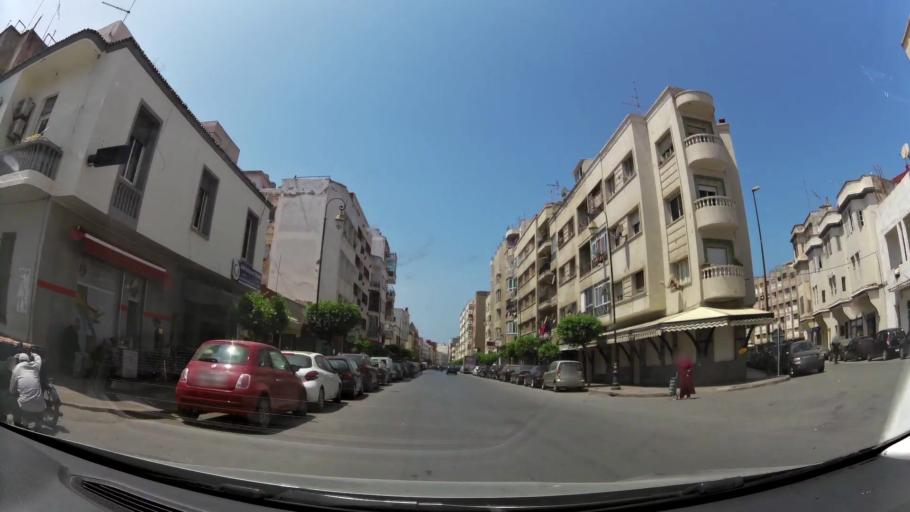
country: MA
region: Rabat-Sale-Zemmour-Zaer
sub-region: Rabat
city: Rabat
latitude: 34.0240
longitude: -6.8478
